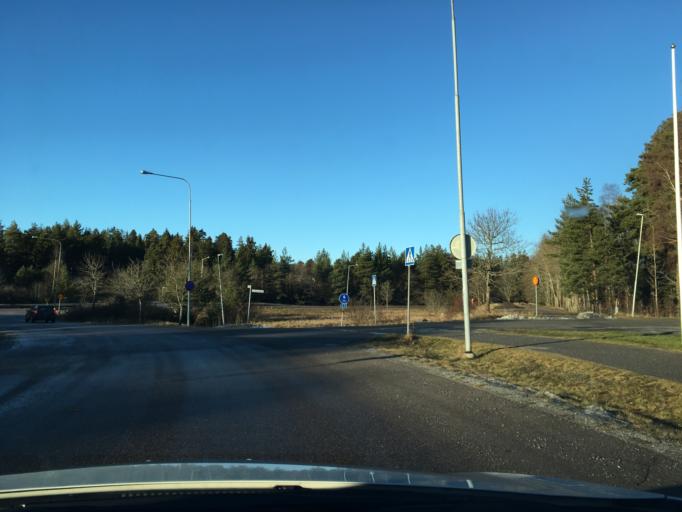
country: SE
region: Uppsala
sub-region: Knivsta Kommun
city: Knivsta
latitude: 59.7265
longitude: 17.7810
